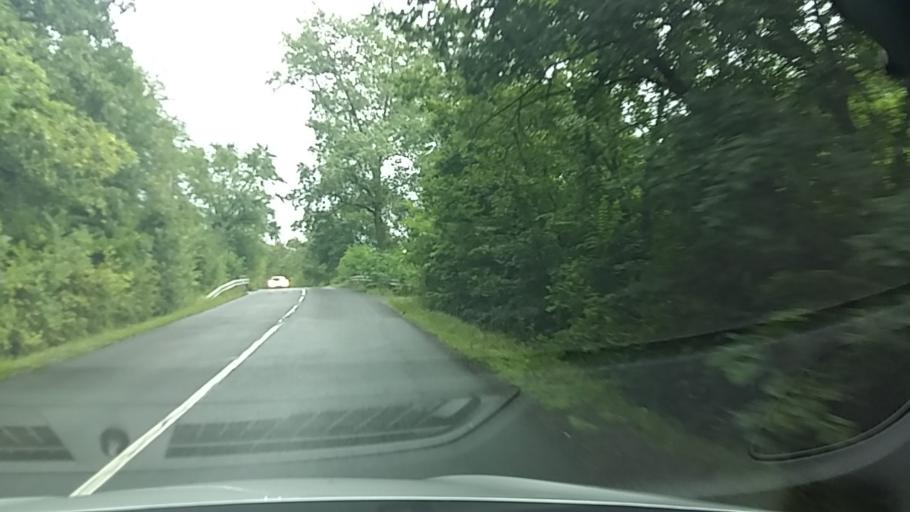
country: HU
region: Pest
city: Szob
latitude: 47.8587
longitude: 18.8009
